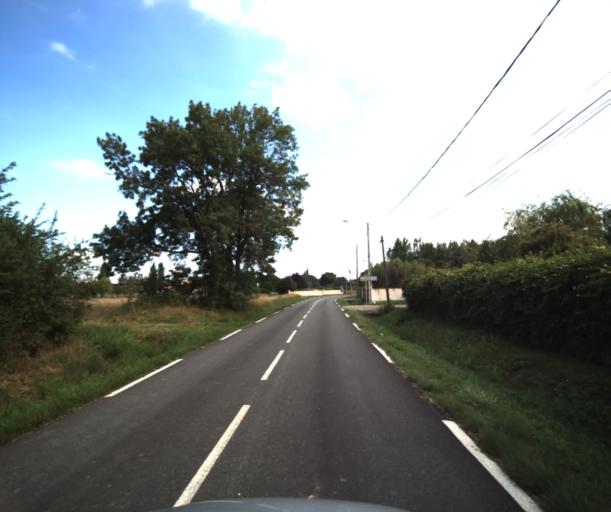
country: FR
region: Midi-Pyrenees
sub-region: Departement de la Haute-Garonne
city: Lacasse
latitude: 43.4000
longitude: 1.2570
